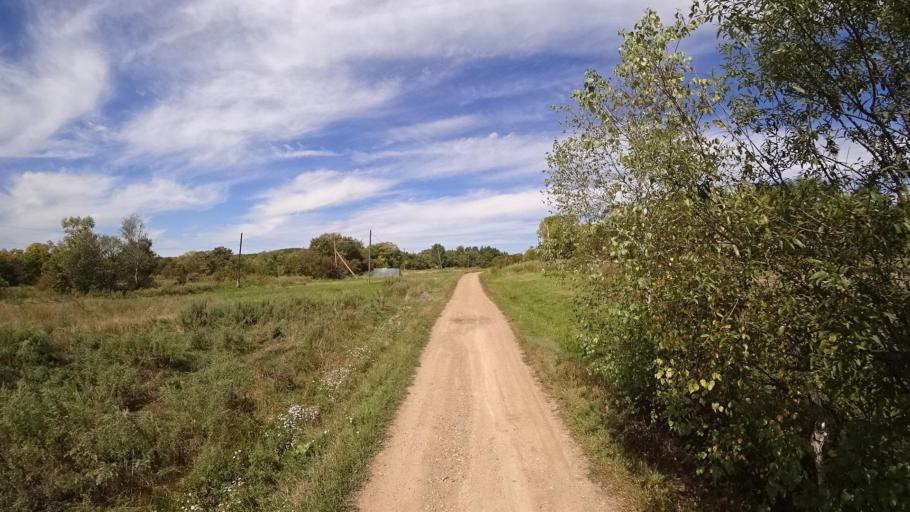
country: RU
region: Primorskiy
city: Yakovlevka
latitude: 44.6471
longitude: 133.5880
